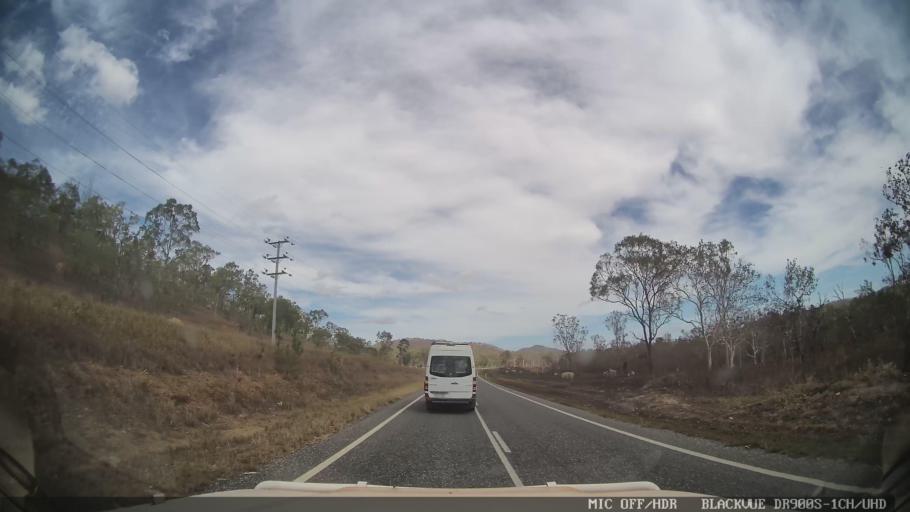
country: AU
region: Queensland
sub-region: Cairns
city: Port Douglas
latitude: -16.7164
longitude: 145.3523
